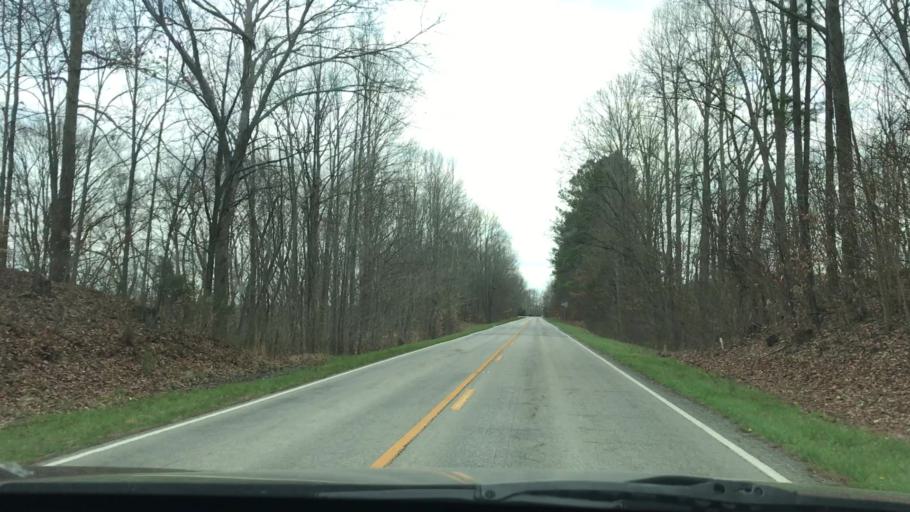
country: US
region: Kentucky
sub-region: Hart County
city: Munfordville
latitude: 37.3089
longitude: -85.7627
